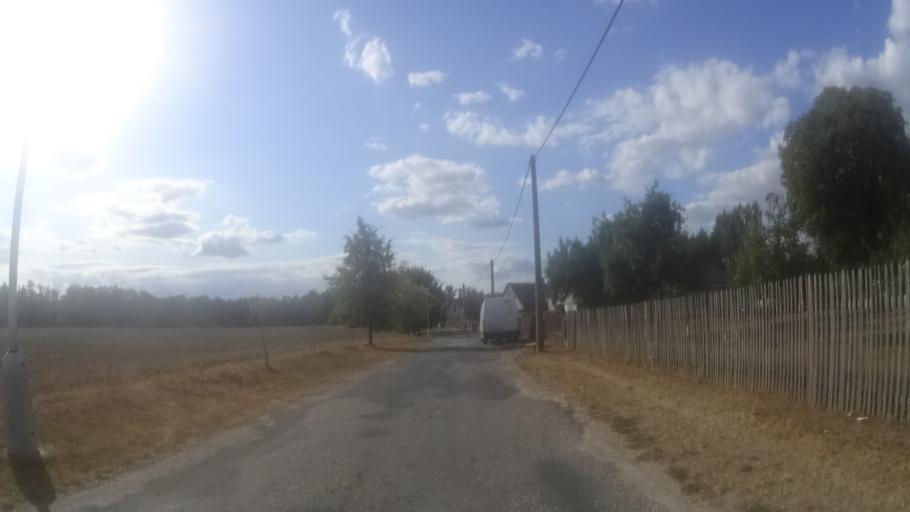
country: CZ
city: Albrechtice nad Orlici
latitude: 50.1560
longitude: 16.0453
